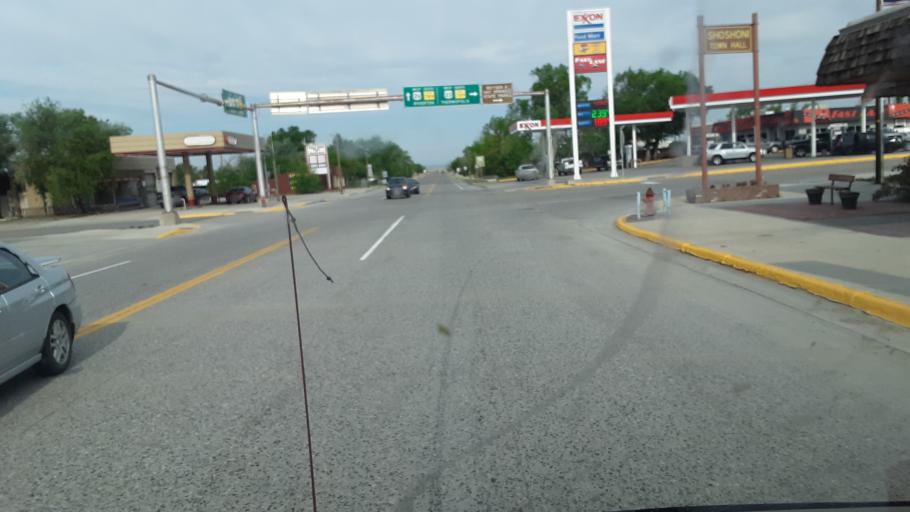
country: US
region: Wyoming
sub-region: Fremont County
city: Riverton
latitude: 43.2356
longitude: -108.1100
